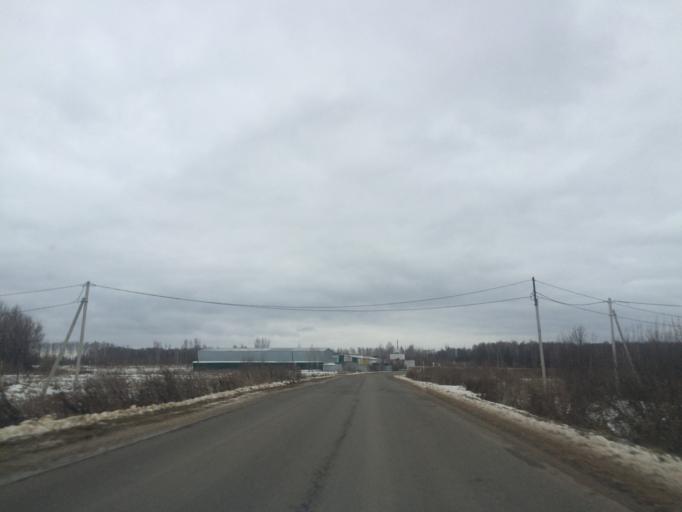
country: RU
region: Tula
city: Kosaya Gora
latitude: 54.1532
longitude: 37.4309
